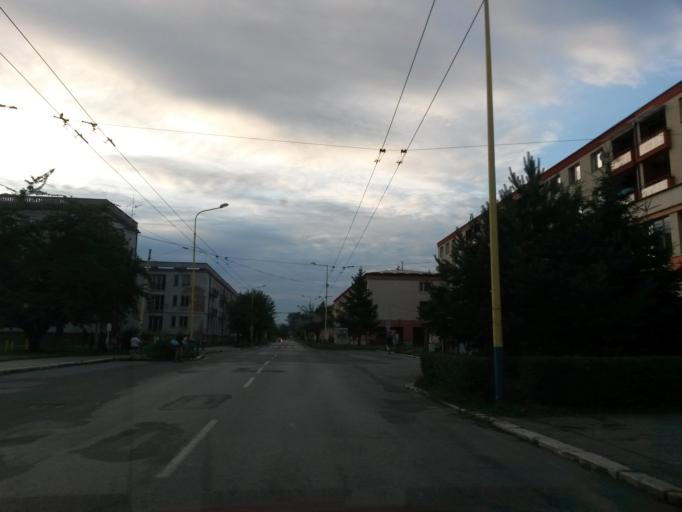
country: SK
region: Presovsky
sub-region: Okres Presov
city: Presov
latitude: 48.9899
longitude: 21.2357
